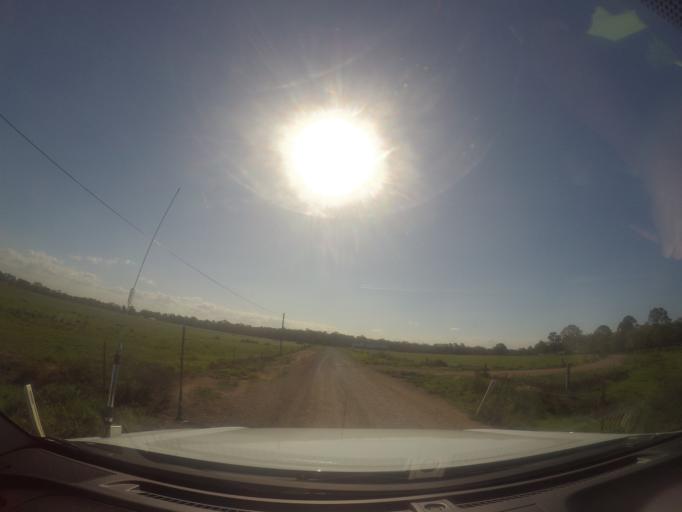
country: AU
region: Queensland
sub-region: Logan
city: Chambers Flat
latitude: -27.7513
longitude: 153.0983
